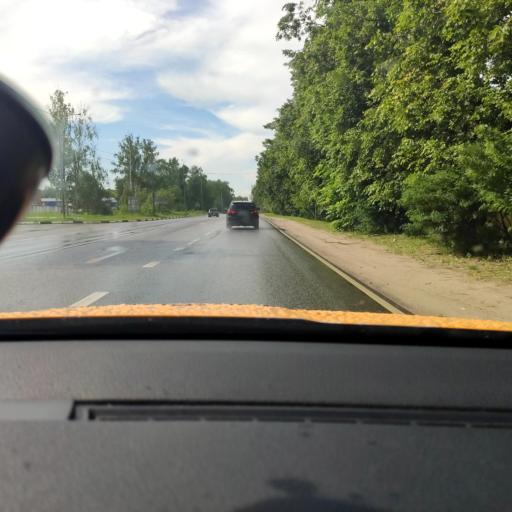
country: RU
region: Moskovskaya
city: Stupino
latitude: 54.9168
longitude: 38.0631
